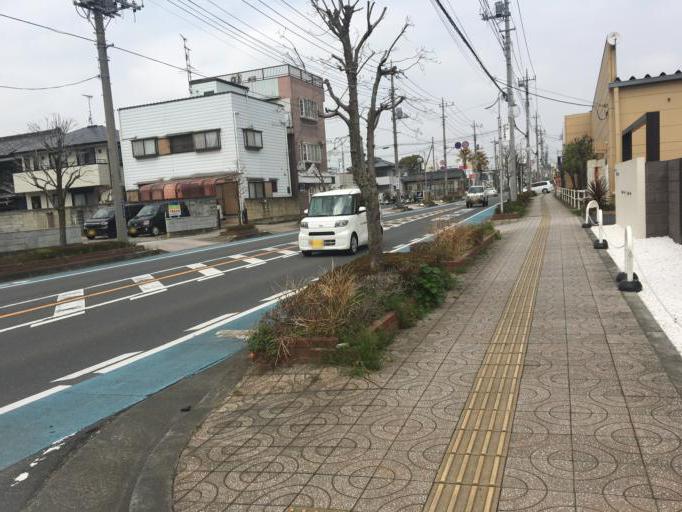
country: JP
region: Saitama
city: Hanyu
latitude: 36.1682
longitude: 139.5395
